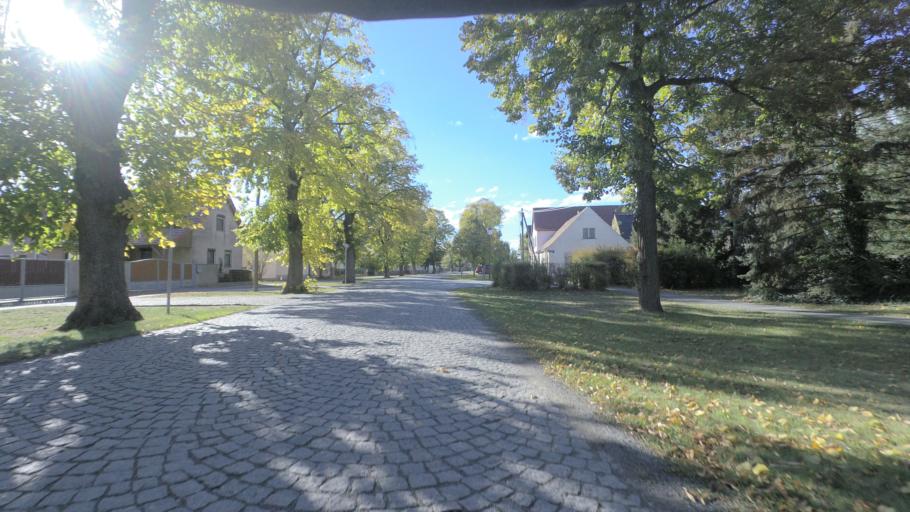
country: DE
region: Saxony
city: Nauwalde
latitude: 51.4553
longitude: 13.3397
